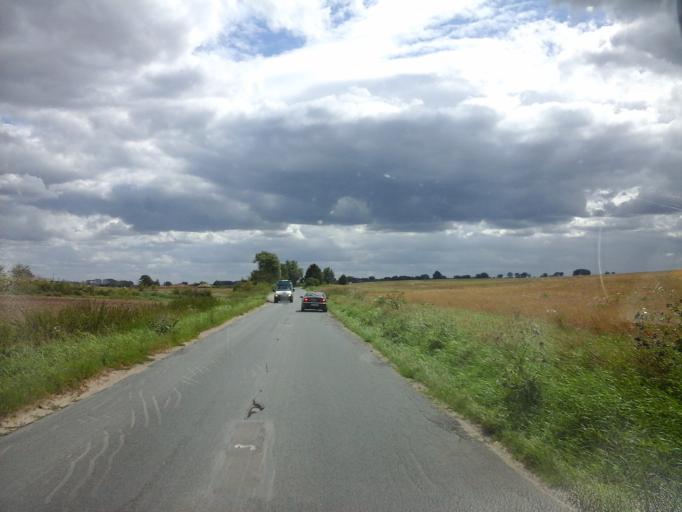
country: PL
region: West Pomeranian Voivodeship
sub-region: Powiat policki
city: Przeclaw
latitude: 53.4074
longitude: 14.4269
